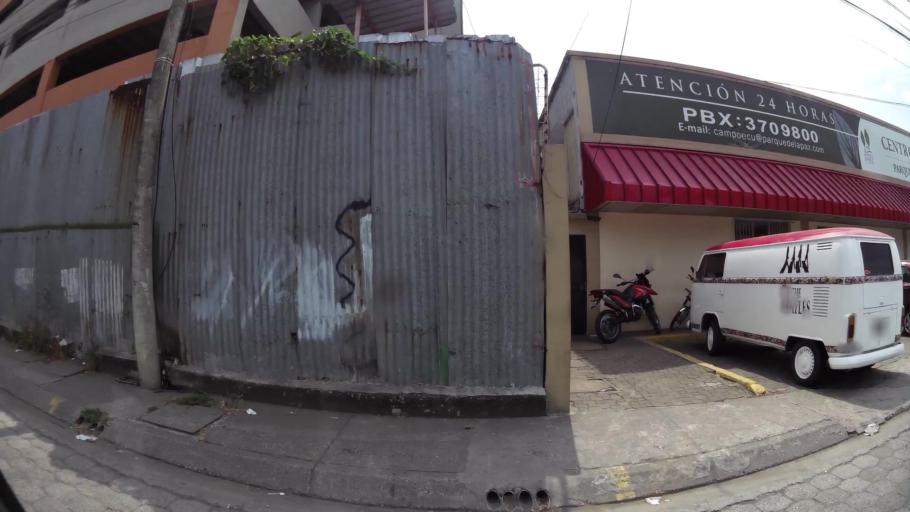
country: EC
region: Guayas
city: Eloy Alfaro
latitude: -2.1356
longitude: -79.9030
